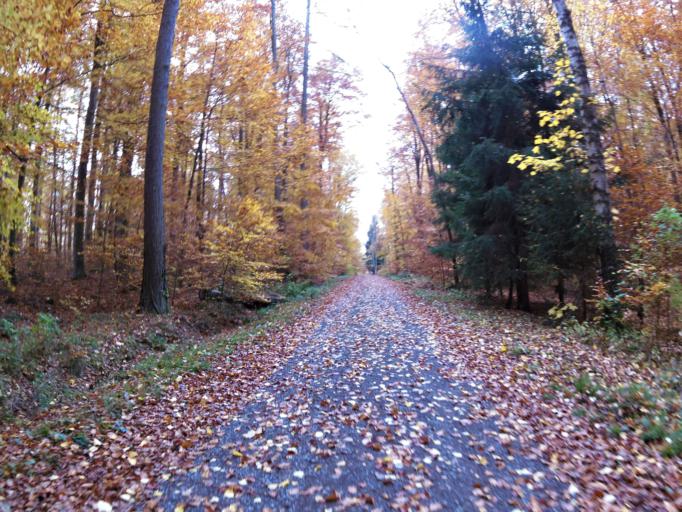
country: DE
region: Bavaria
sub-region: Regierungsbezirk Unterfranken
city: Kist
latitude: 49.7321
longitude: 9.8291
